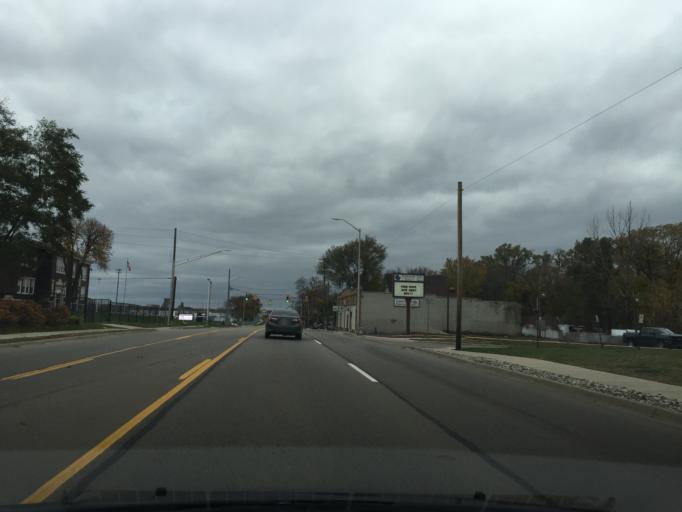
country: US
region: Michigan
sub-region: Oakland County
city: Pontiac
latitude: 42.6482
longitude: -83.3040
